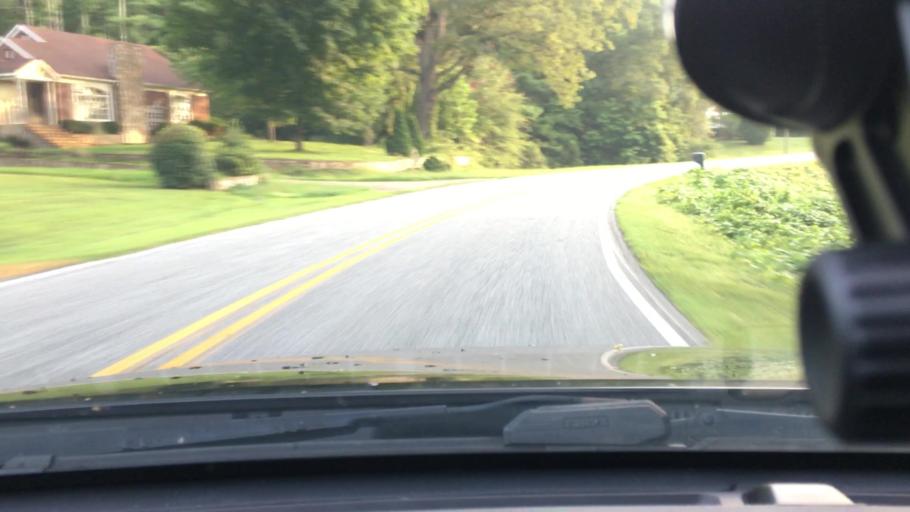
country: US
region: North Carolina
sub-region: Rutherford County
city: Rutherfordton
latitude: 35.3881
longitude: -81.9851
